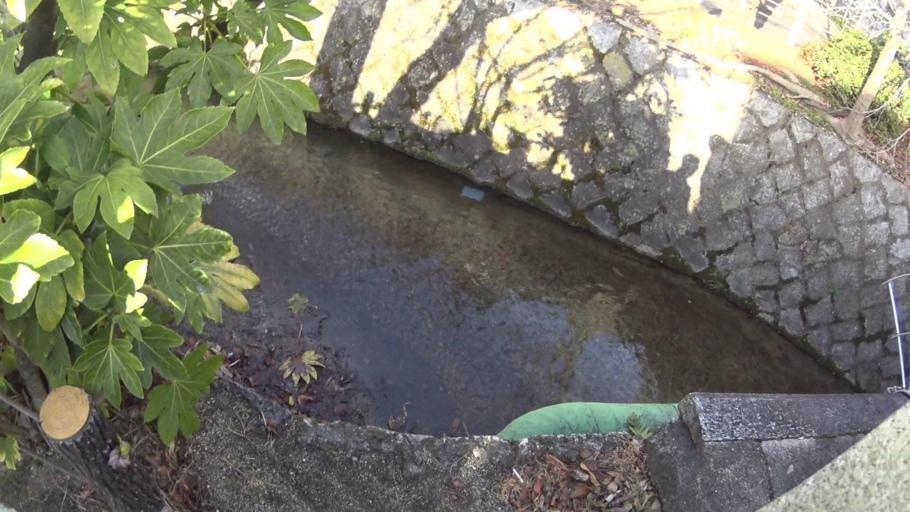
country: JP
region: Kyoto
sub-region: Kyoto-shi
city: Kamigyo-ku
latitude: 35.0248
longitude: 135.8007
